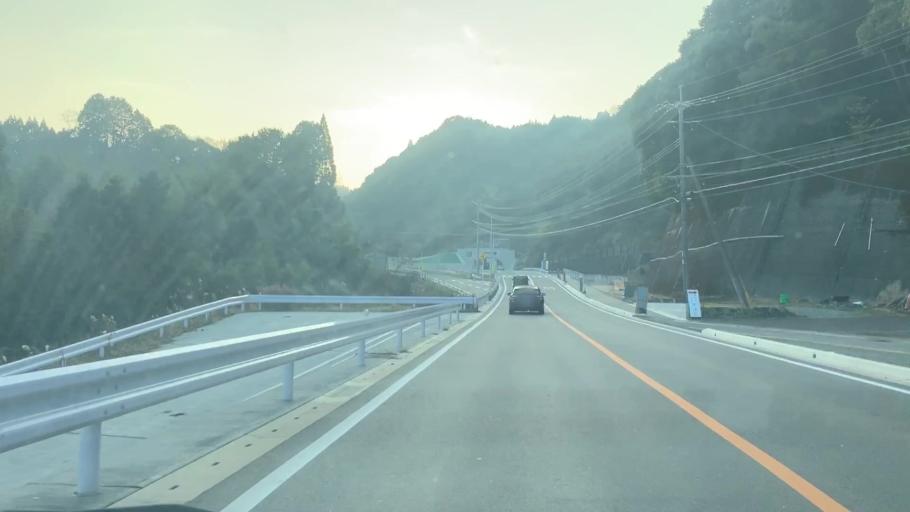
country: JP
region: Saga Prefecture
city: Takeocho-takeo
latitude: 33.2621
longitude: 130.0314
